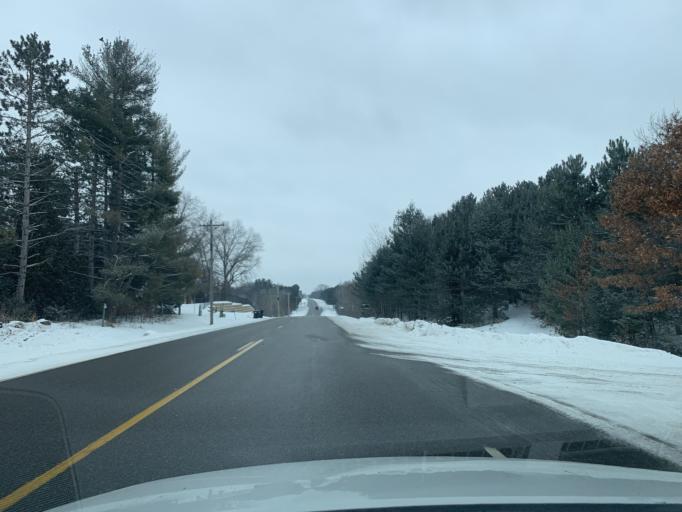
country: US
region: Minnesota
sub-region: Sherburne County
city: Zimmerman
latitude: 45.5013
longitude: -93.6189
